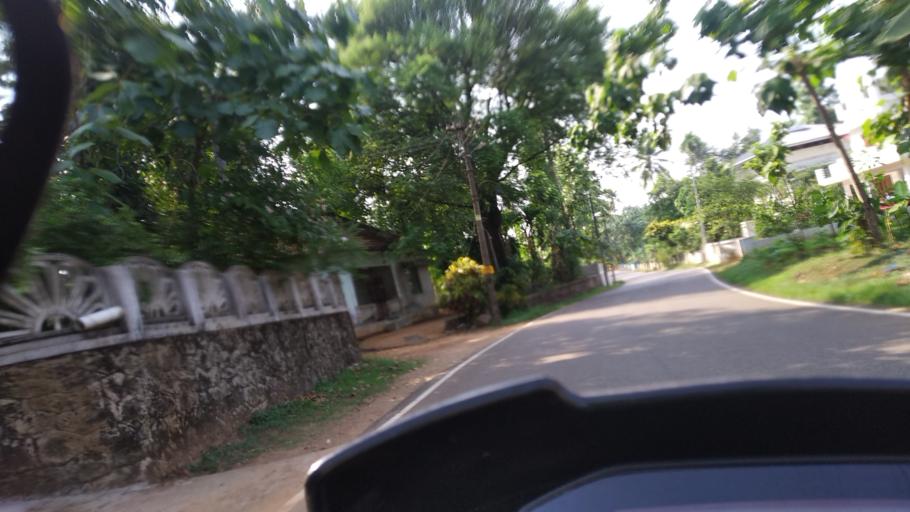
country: IN
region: Kerala
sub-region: Ernakulam
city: Piravam
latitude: 9.8642
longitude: 76.5132
